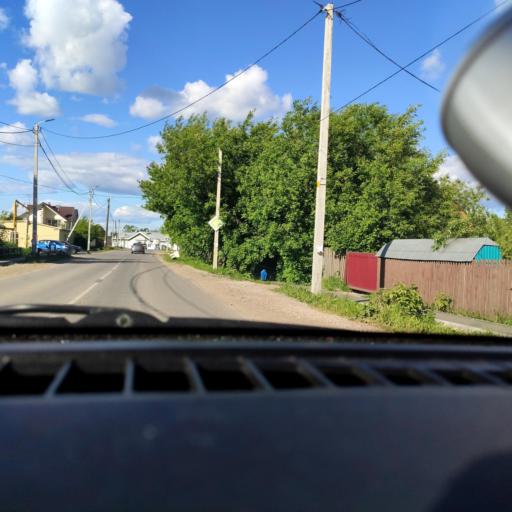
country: RU
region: Perm
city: Novyye Lyady
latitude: 58.0517
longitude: 56.5987
